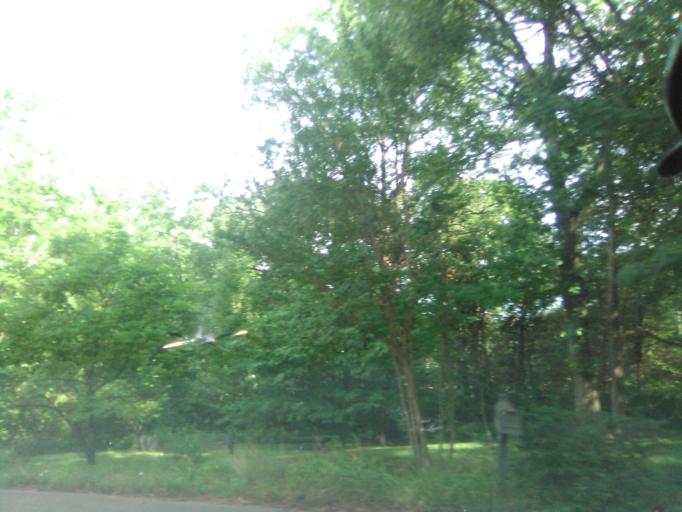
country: US
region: Tennessee
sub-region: Davidson County
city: Belle Meade
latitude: 36.1103
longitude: -86.8989
